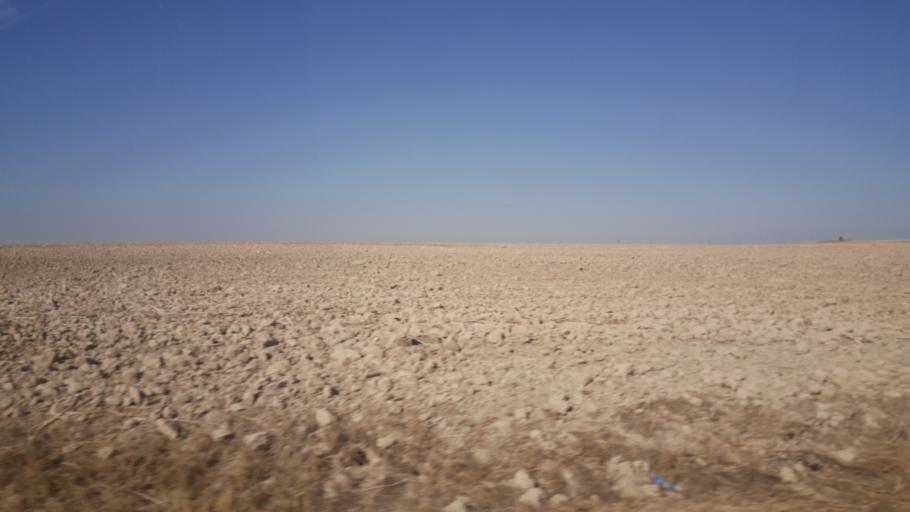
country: TR
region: Konya
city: Celtik
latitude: 39.0610
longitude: 31.8690
